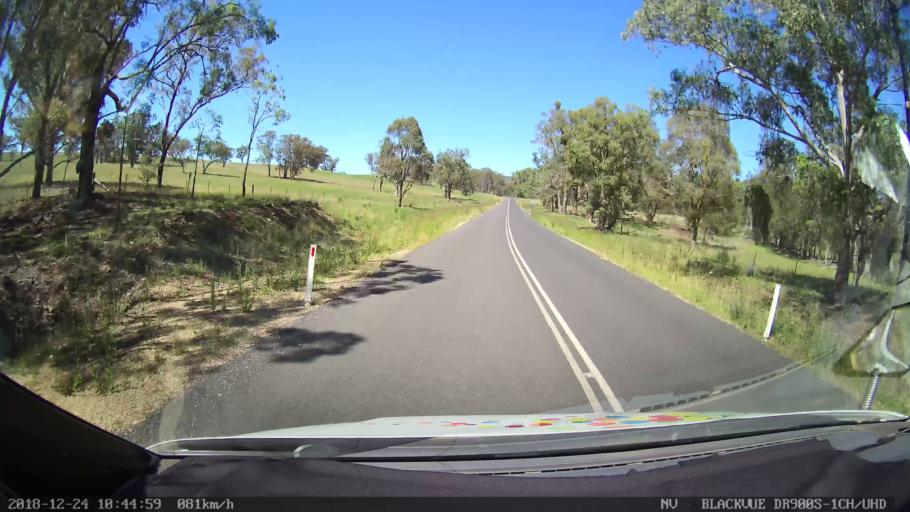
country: AU
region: New South Wales
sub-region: Upper Hunter Shire
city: Merriwa
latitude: -31.8985
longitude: 150.4397
